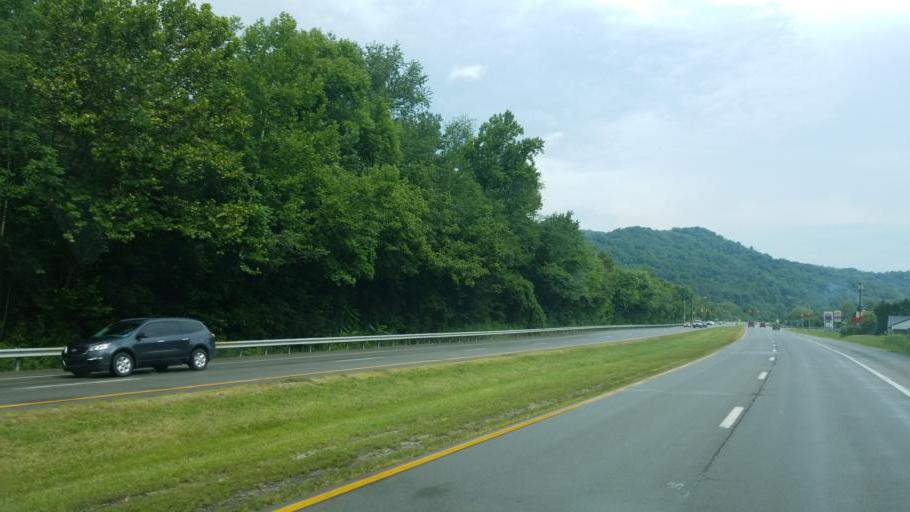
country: US
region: West Virginia
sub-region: Logan County
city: Chapmanville
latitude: 37.9615
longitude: -82.0215
